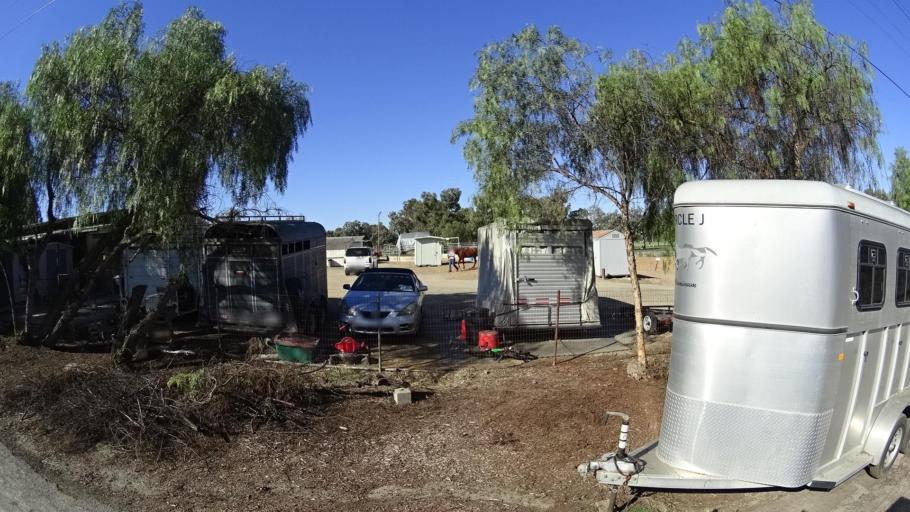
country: US
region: California
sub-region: San Diego County
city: Bonita
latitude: 32.6798
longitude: -117.0088
